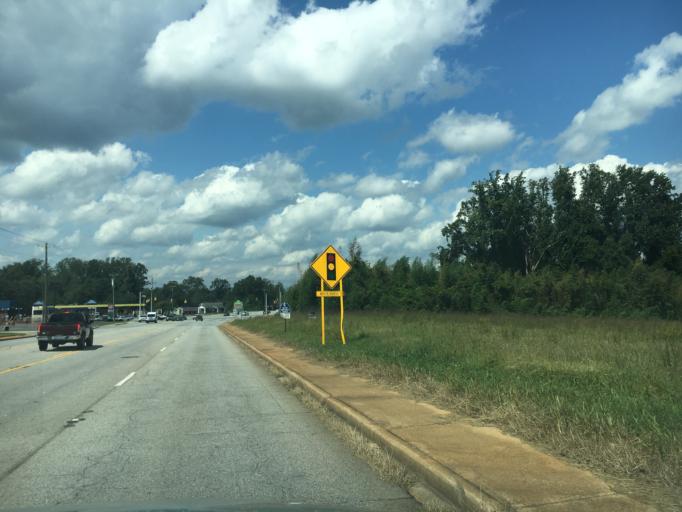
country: US
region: South Carolina
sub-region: Greenville County
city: Berea
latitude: 34.8890
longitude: -82.4660
